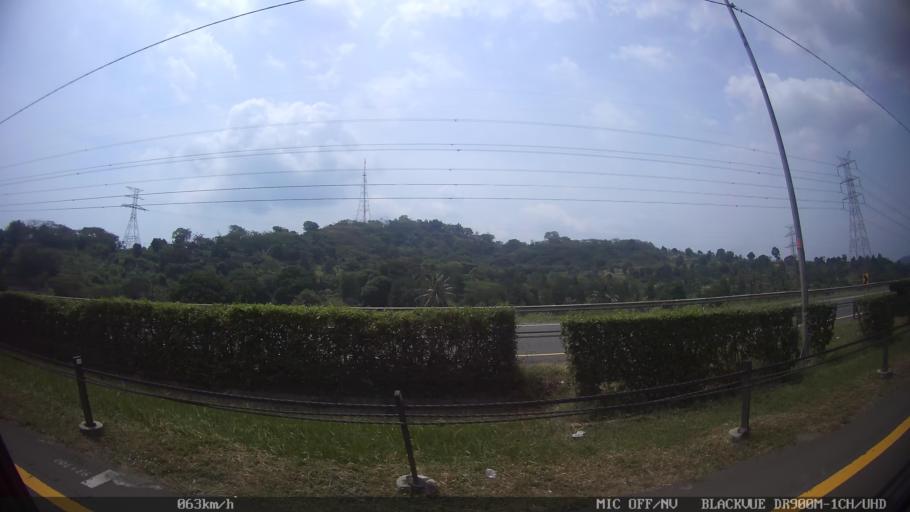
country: ID
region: Banten
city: Curug
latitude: -5.9901
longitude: 106.0460
